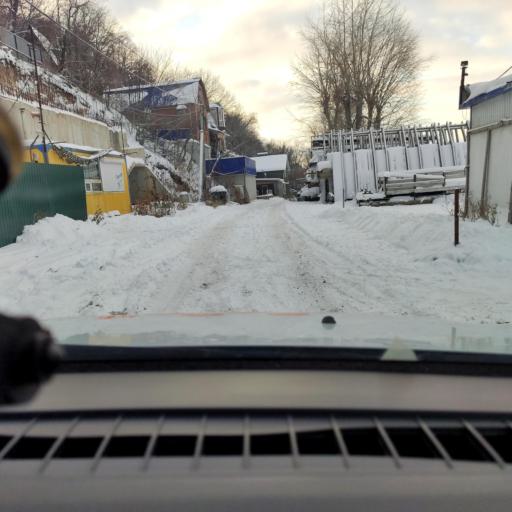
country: RU
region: Samara
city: Samara
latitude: 53.2868
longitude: 50.1908
